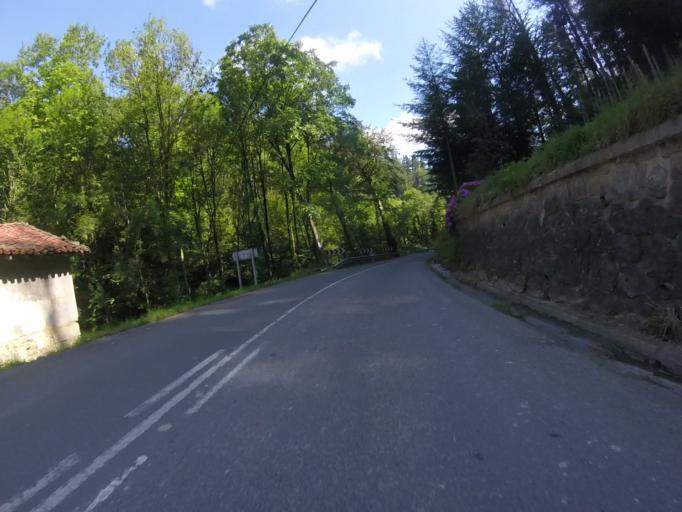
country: ES
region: Basque Country
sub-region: Provincia de Guipuzcoa
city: Beizama
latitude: 43.0995
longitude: -2.2442
